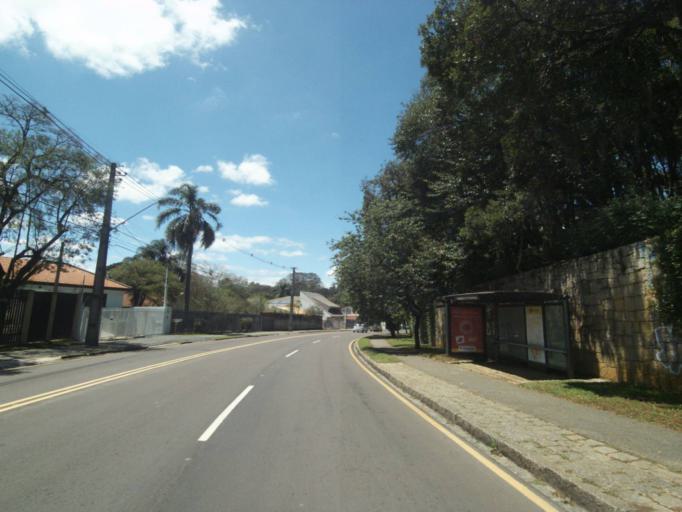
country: BR
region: Parana
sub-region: Curitiba
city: Curitiba
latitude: -25.3873
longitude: -49.2694
